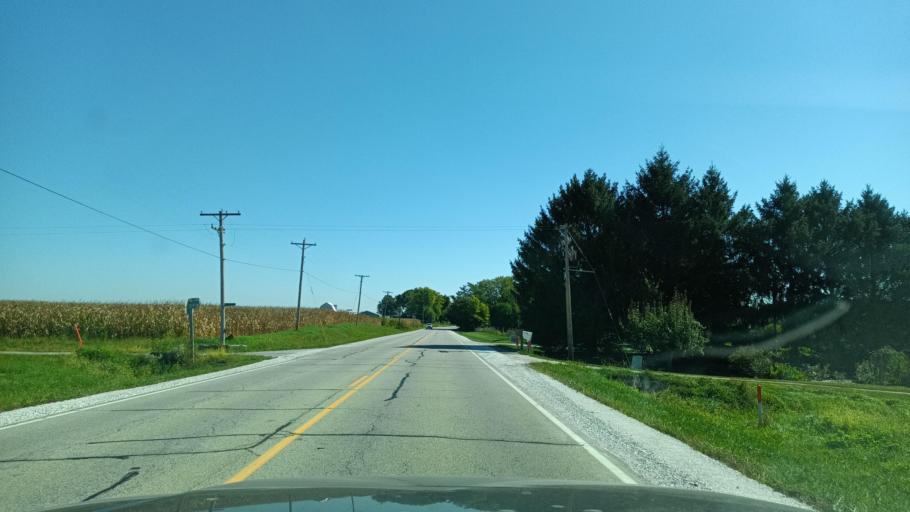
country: US
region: Illinois
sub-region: Peoria County
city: Hanna City
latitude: 40.7945
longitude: -89.7809
